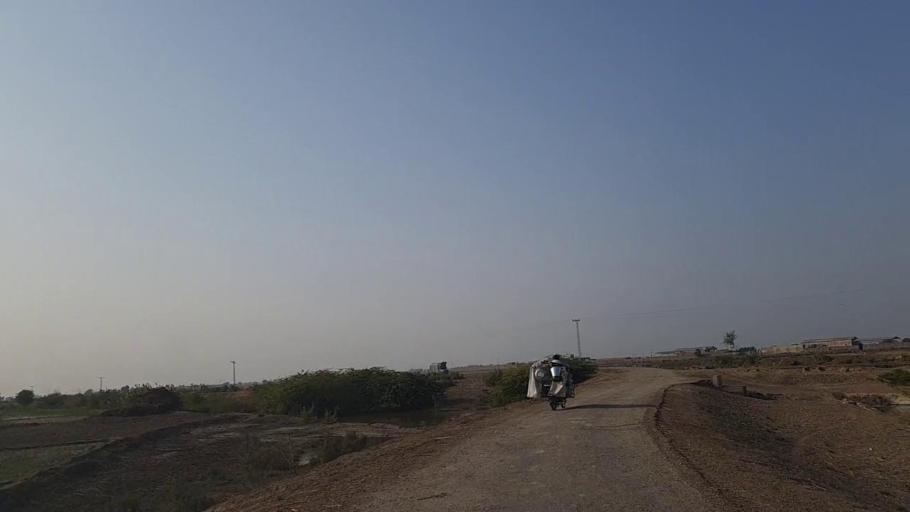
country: PK
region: Sindh
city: Jam Sahib
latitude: 26.2858
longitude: 68.6106
